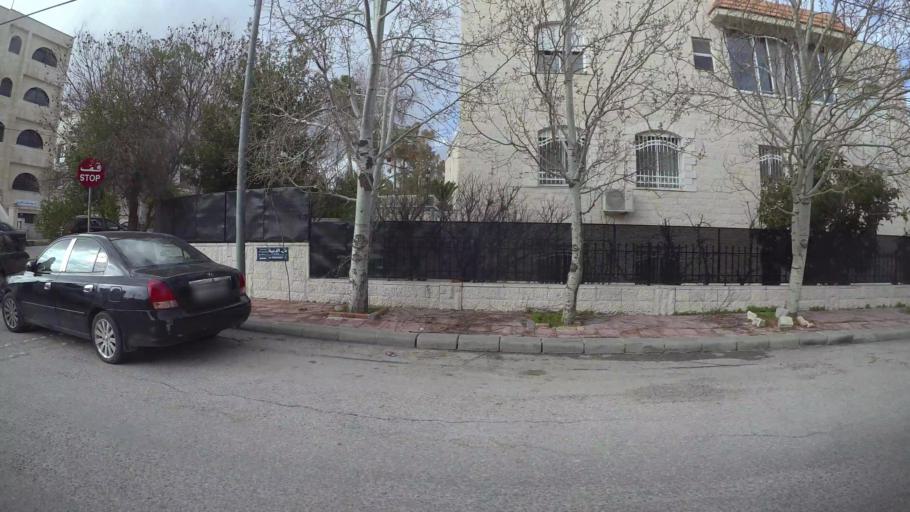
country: JO
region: Amman
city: Wadi as Sir
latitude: 31.9789
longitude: 35.8436
